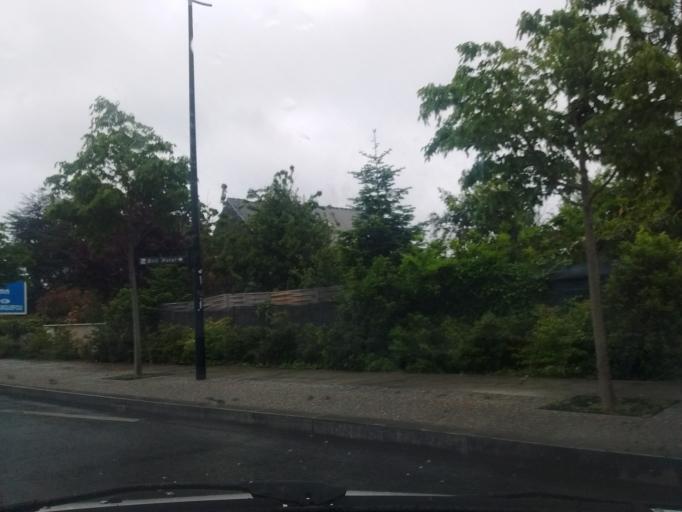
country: FR
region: Pays de la Loire
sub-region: Departement de la Loire-Atlantique
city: Nantes
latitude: 47.2542
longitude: -1.5298
